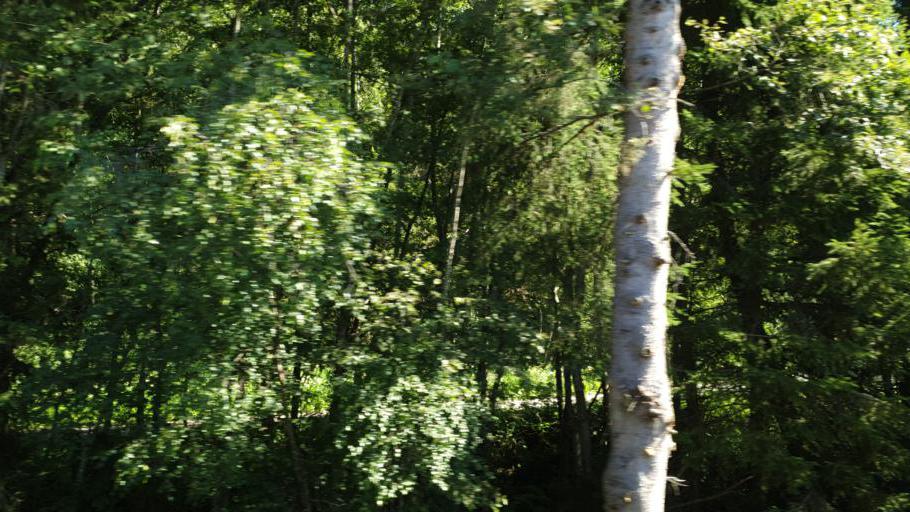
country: NO
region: Sor-Trondelag
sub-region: Meldal
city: Meldal
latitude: 63.1811
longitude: 9.7671
